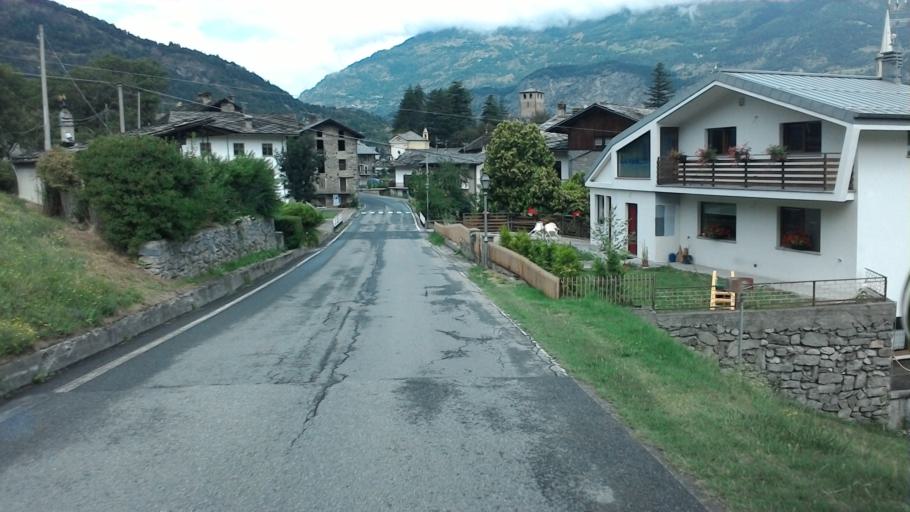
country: IT
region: Aosta Valley
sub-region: Valle d'Aosta
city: Plan d'Introd
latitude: 45.6892
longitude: 7.1891
